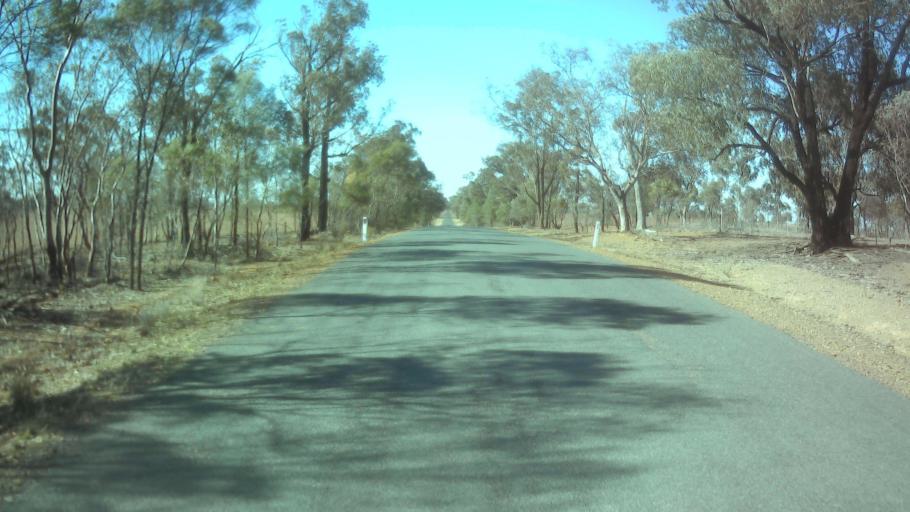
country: AU
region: New South Wales
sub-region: Forbes
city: Forbes
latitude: -33.7049
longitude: 147.8058
